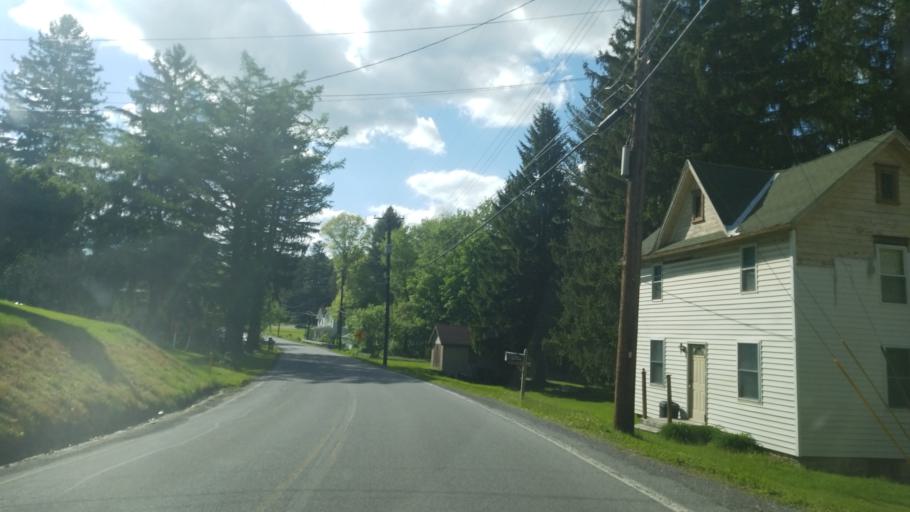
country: US
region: Pennsylvania
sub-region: Clearfield County
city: Troy
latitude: 40.9281
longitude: -78.2810
